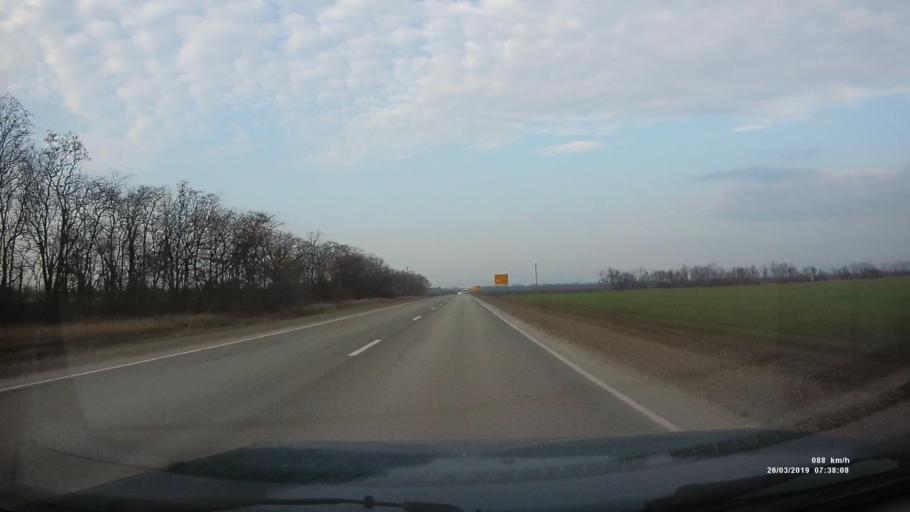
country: RU
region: Rostov
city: Novobessergenovka
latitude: 47.2005
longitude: 38.6885
